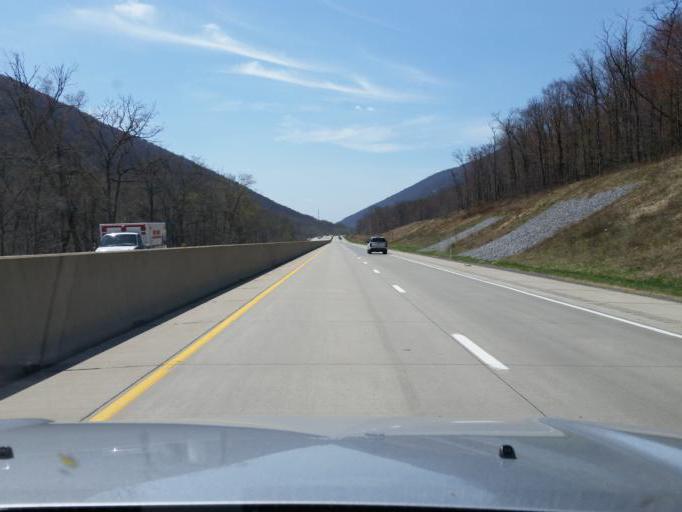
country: US
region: Pennsylvania
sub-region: Juniata County
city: Mifflintown
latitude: 40.6091
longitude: -77.4589
